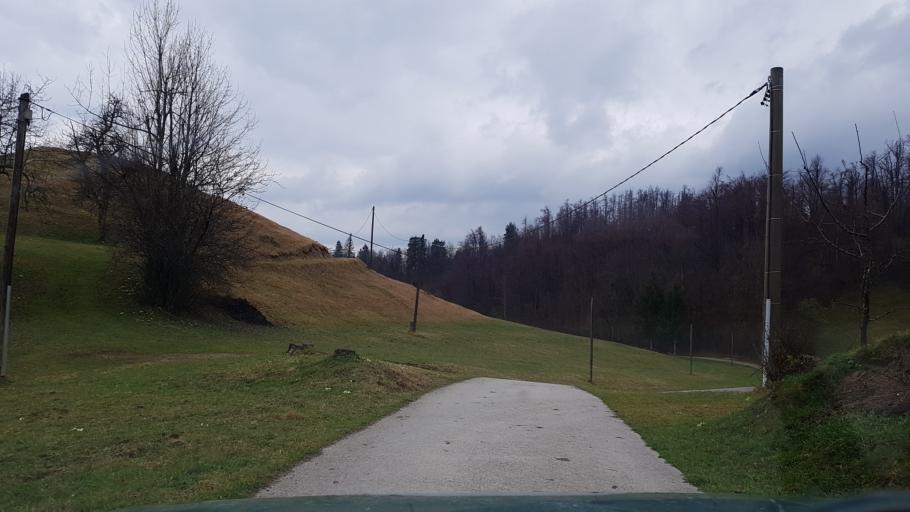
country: SI
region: Cerkno
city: Cerkno
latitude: 46.1353
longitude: 13.8574
